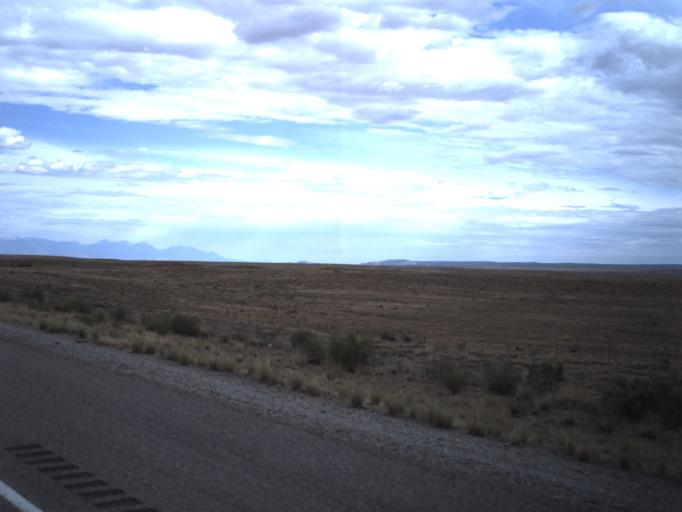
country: US
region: Utah
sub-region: Grand County
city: Moab
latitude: 38.9238
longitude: -109.9767
